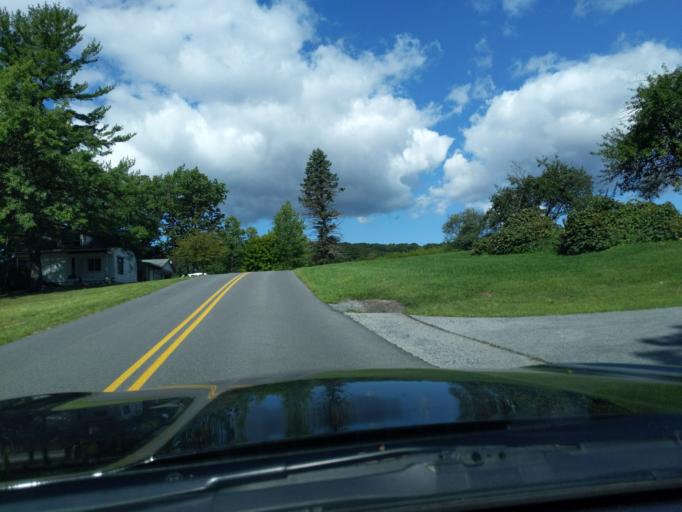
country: US
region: Pennsylvania
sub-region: Blair County
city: Altoona
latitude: 40.5463
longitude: -78.4017
